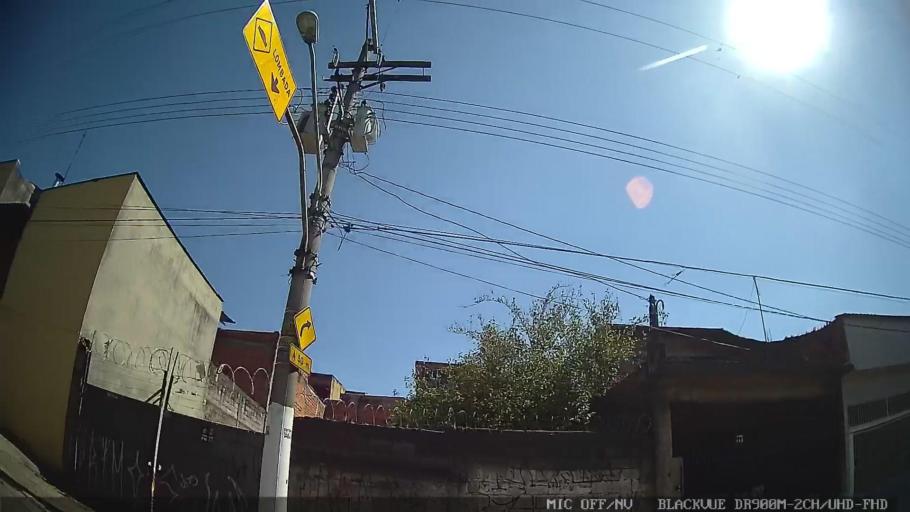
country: BR
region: Sao Paulo
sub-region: Sao Caetano Do Sul
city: Sao Caetano do Sul
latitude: -23.6034
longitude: -46.4879
